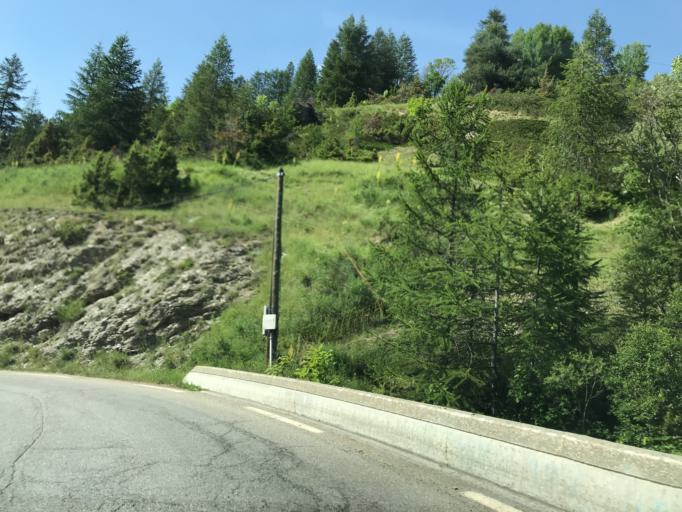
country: IT
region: Piedmont
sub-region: Provincia di Torino
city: Sauze di Cesana
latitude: 44.7508
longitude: 6.8330
